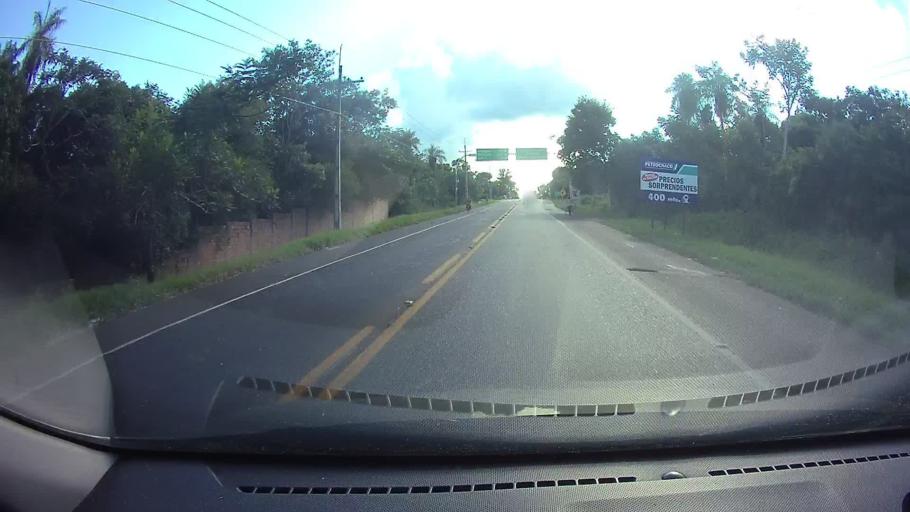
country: PY
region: Cordillera
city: Eusebio Ayala
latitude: -25.3813
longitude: -57.0421
